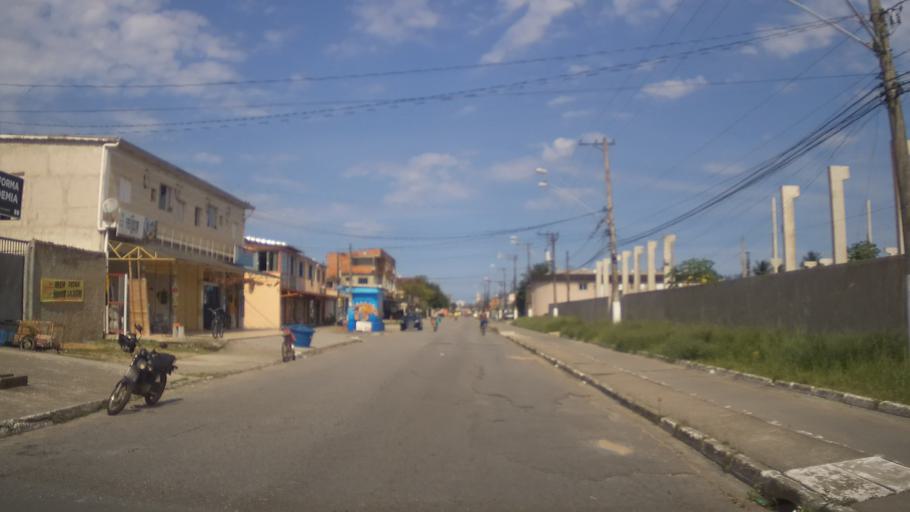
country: BR
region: Sao Paulo
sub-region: Praia Grande
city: Praia Grande
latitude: -23.9971
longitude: -46.4549
